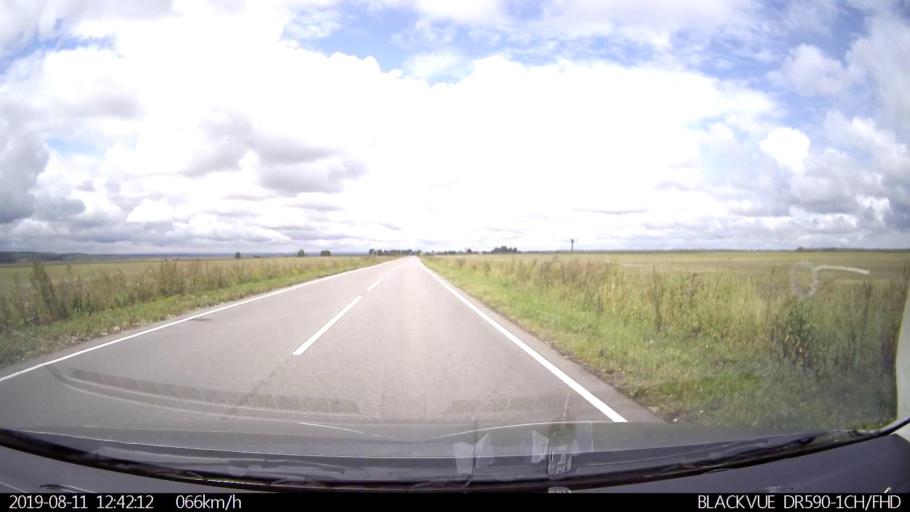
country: RU
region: Ulyanovsk
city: Ignatovka
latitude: 53.8441
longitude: 47.7543
